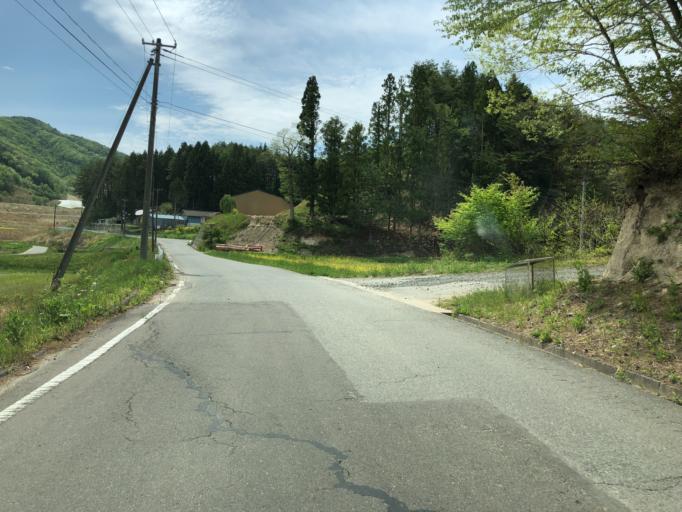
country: JP
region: Fukushima
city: Yanagawamachi-saiwaicho
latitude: 37.7200
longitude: 140.7178
